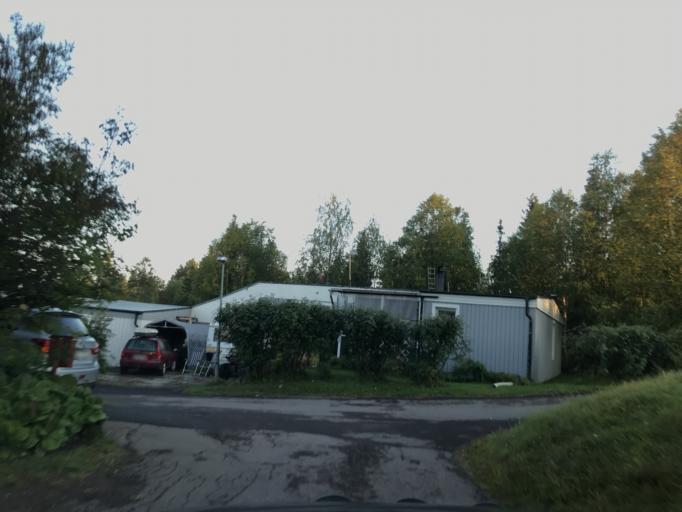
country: SE
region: Norrbotten
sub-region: Gallivare Kommun
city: Malmberget
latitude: 67.6484
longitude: 21.0498
